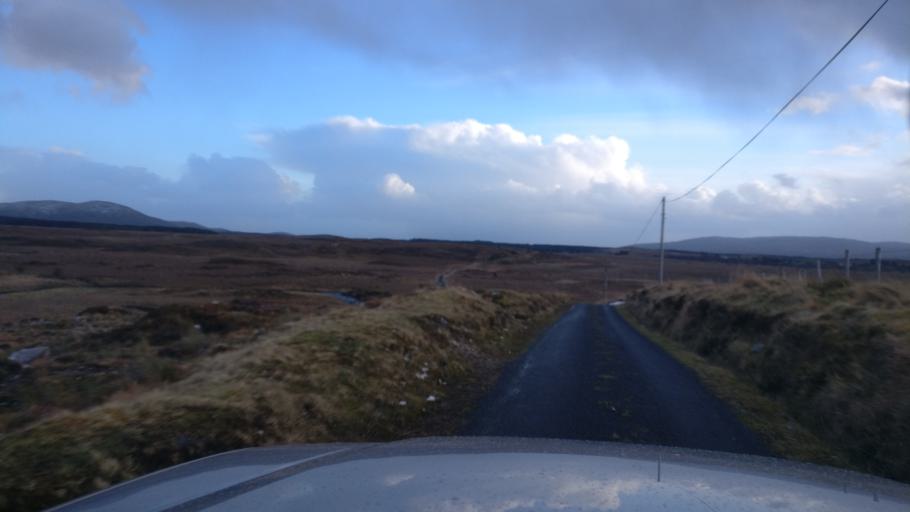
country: IE
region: Connaught
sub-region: County Galway
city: Clifden
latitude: 53.4815
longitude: -9.6960
